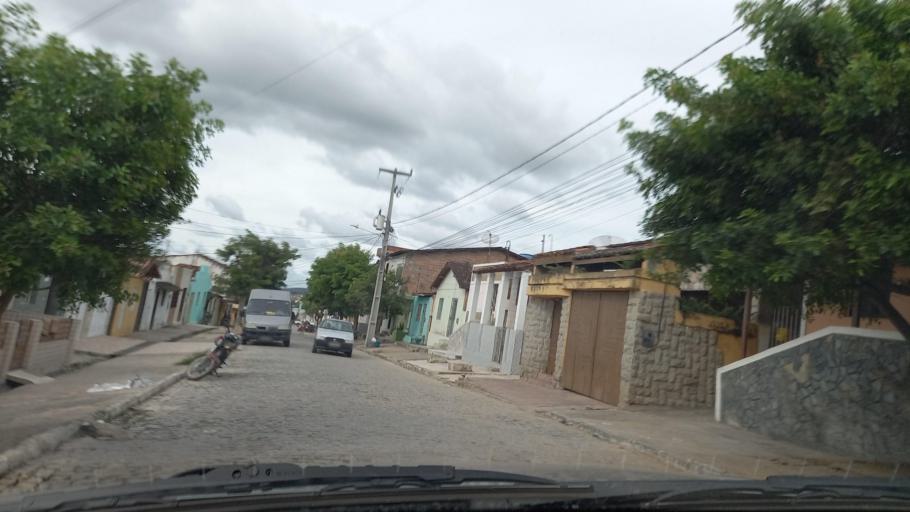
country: BR
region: Pernambuco
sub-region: Gravata
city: Gravata
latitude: -8.2086
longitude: -35.5724
